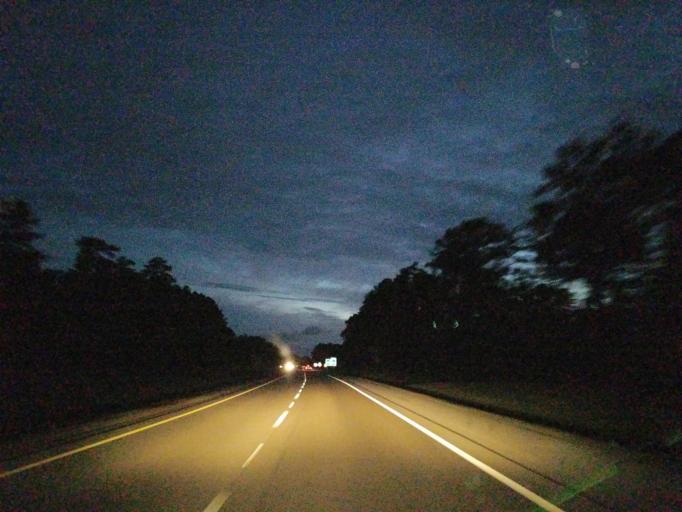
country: US
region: Mississippi
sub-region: Jones County
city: Laurel
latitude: 31.7271
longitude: -89.1010
